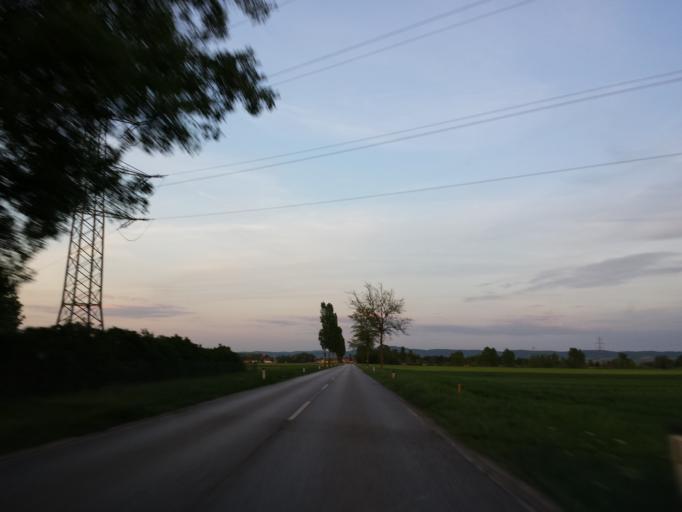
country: AT
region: Lower Austria
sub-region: Politischer Bezirk Tulln
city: Langenrohr
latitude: 48.3226
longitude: 15.9865
